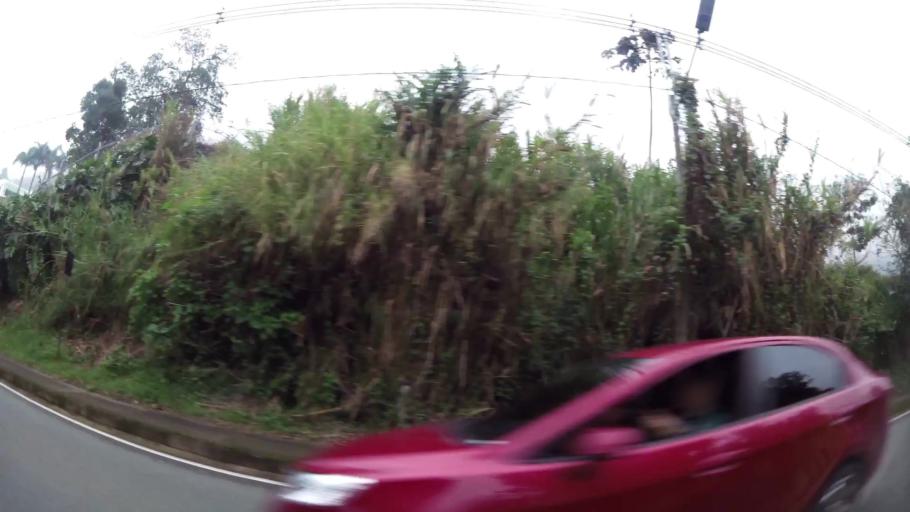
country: CO
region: Antioquia
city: Envigado
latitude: 6.1845
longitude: -75.5475
